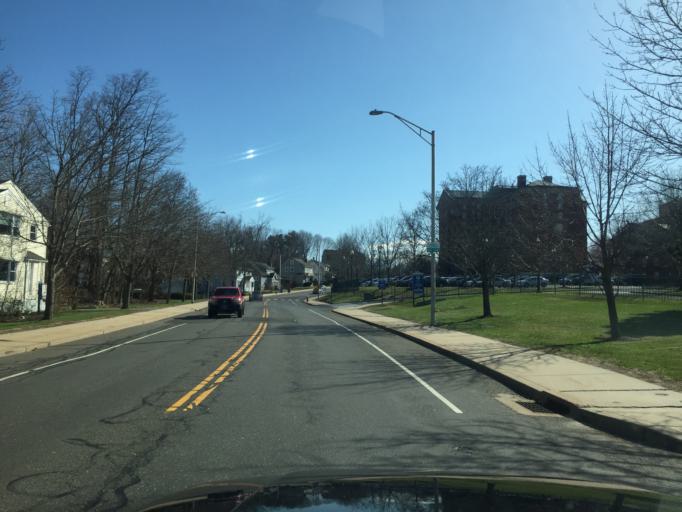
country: US
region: Connecticut
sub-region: Hartford County
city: New Britain
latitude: 41.6903
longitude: -72.7656
